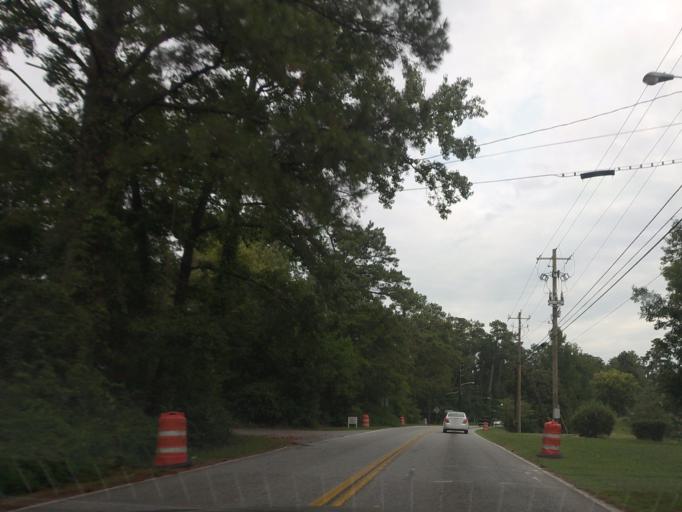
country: US
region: Georgia
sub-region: Bibb County
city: Macon
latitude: 32.8726
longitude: -83.6911
